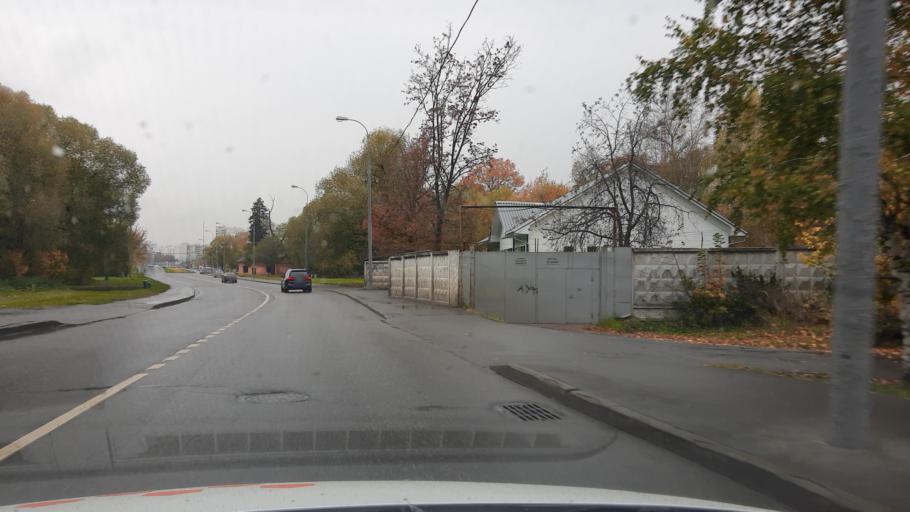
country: RU
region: Moskovskaya
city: Shcherbinka
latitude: 55.5395
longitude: 37.5622
